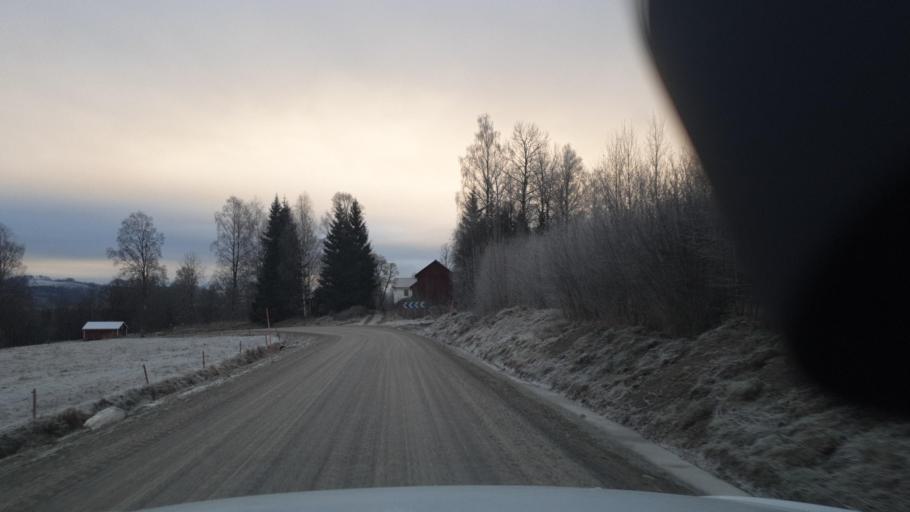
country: SE
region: Vaermland
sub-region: Torsby Kommun
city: Torsby
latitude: 59.9494
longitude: 12.8959
